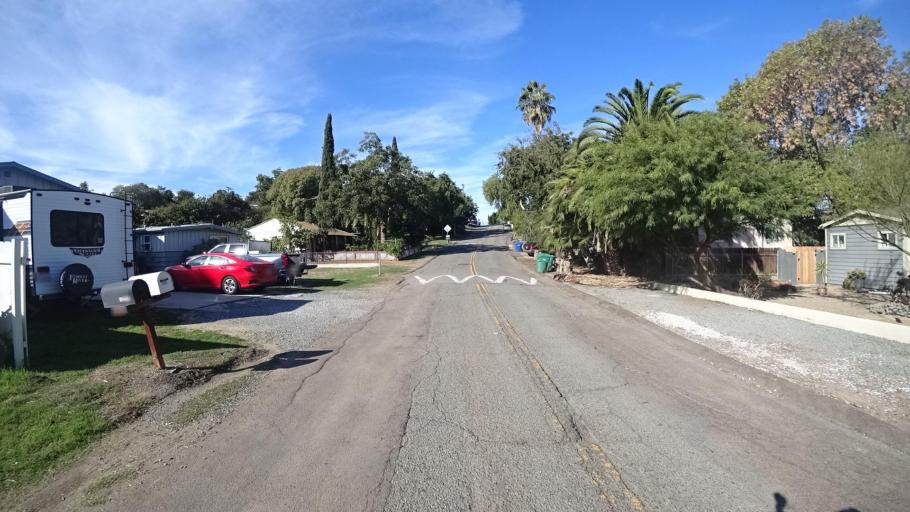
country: US
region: California
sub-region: San Diego County
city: Casa de Oro-Mount Helix
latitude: 32.7421
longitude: -116.9674
